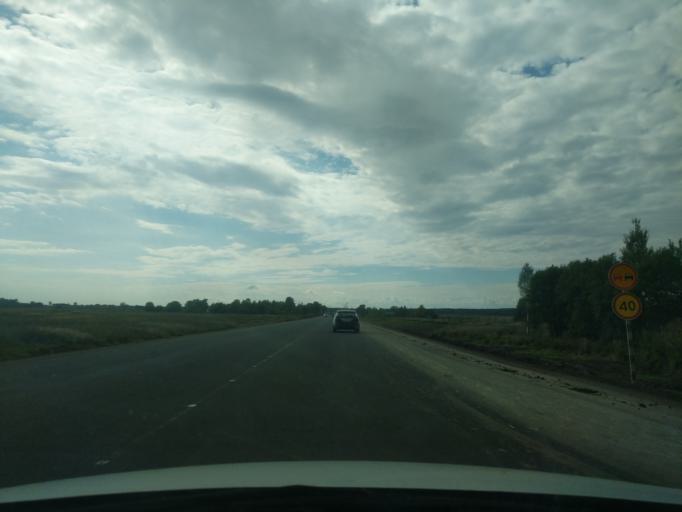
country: RU
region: Kostroma
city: Sudislavl'
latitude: 57.8372
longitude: 41.5595
